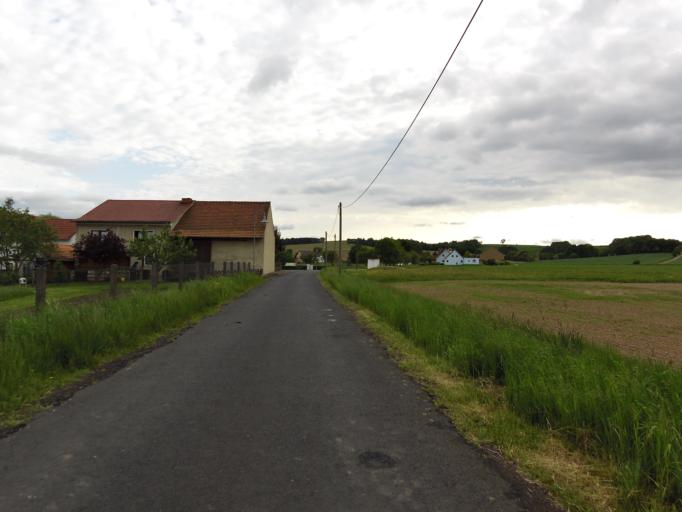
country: DE
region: Thuringia
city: Gerstungen
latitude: 50.9278
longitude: 10.0865
